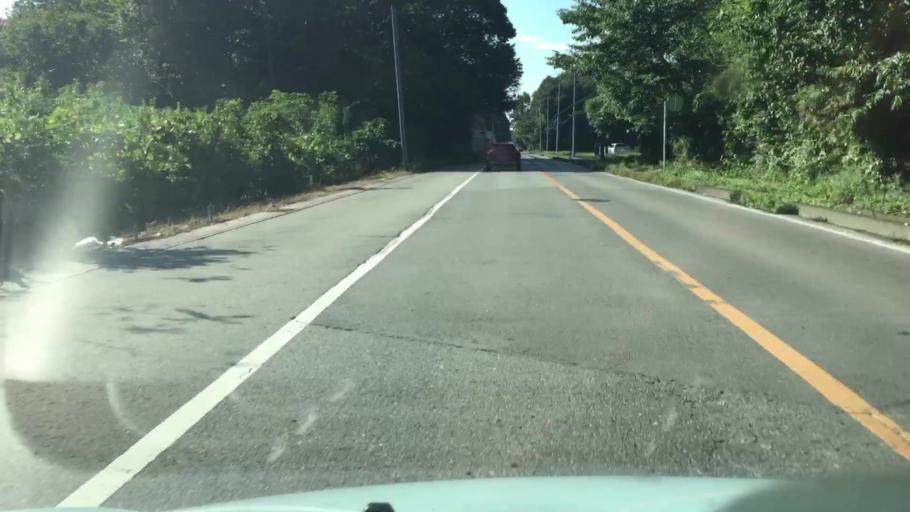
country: JP
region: Tochigi
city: Utsunomiya-shi
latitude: 36.5742
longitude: 139.9791
